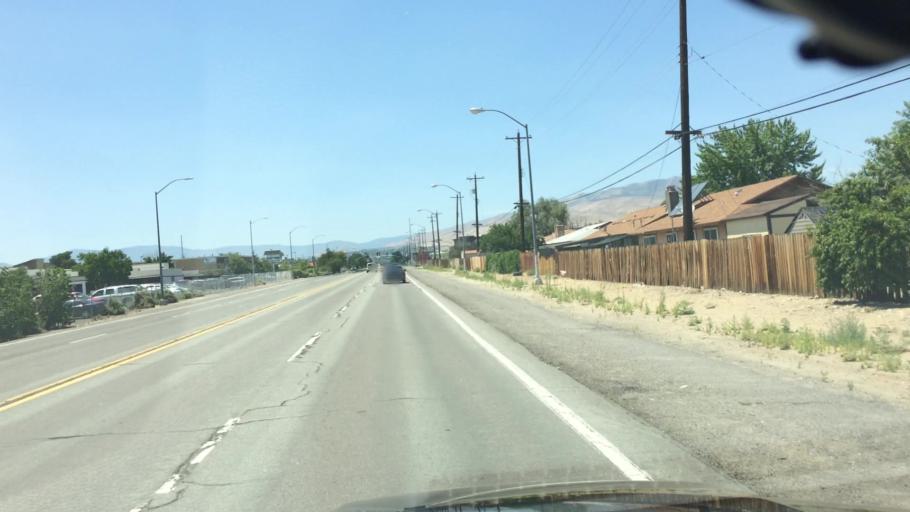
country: US
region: Nevada
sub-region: Washoe County
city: Sparks
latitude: 39.5455
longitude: -119.7665
